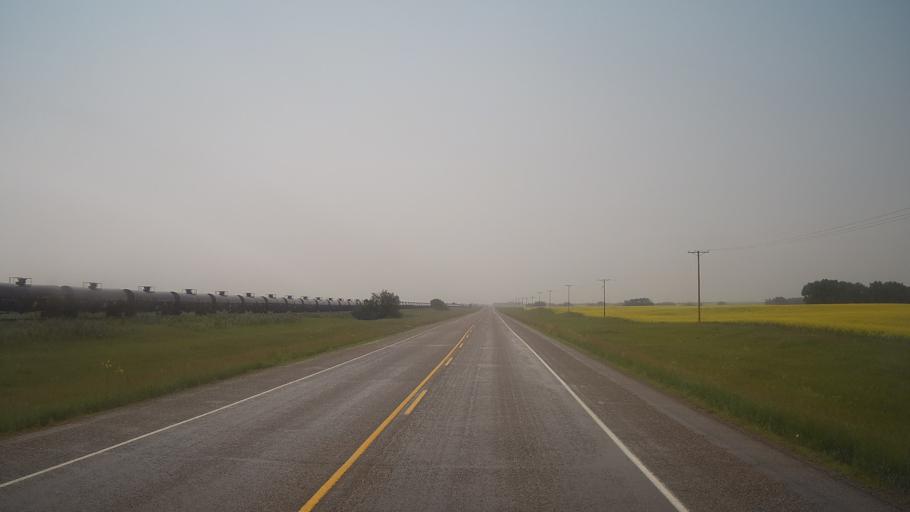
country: CA
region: Saskatchewan
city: Biggar
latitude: 52.1584
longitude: -108.2683
